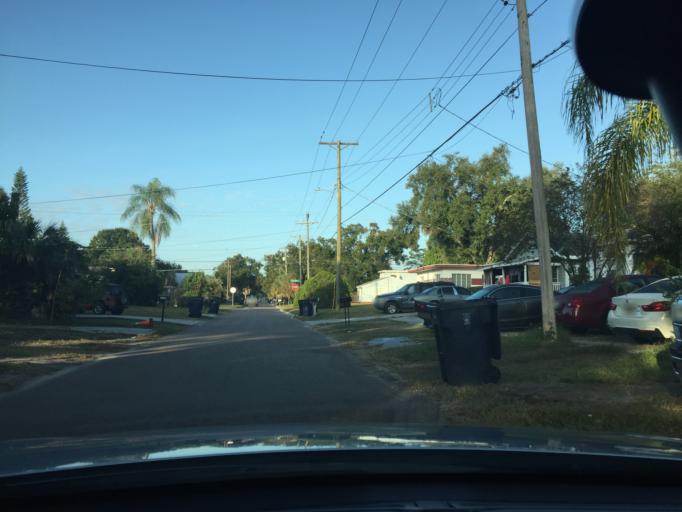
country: US
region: Florida
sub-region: Hillsborough County
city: Tampa
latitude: 27.9535
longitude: -82.4780
